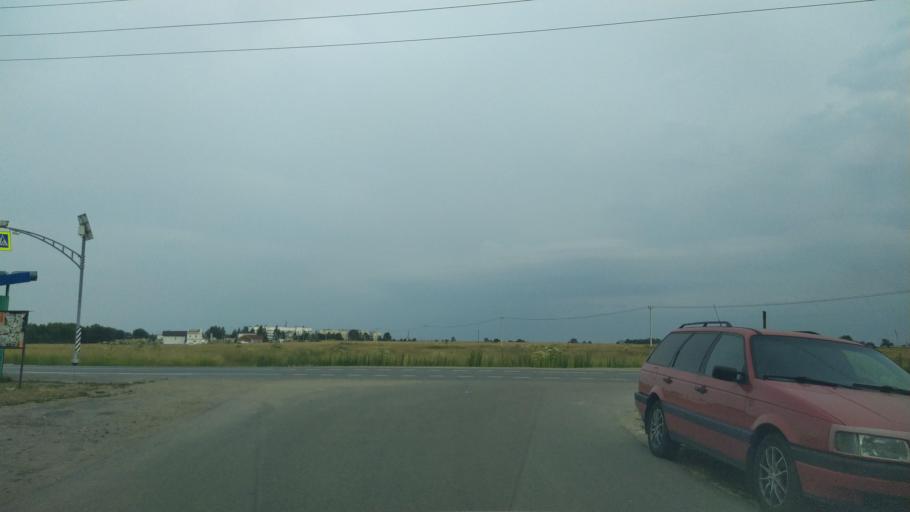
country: RU
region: Leningrad
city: Koltushi
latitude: 59.8905
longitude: 30.7331
